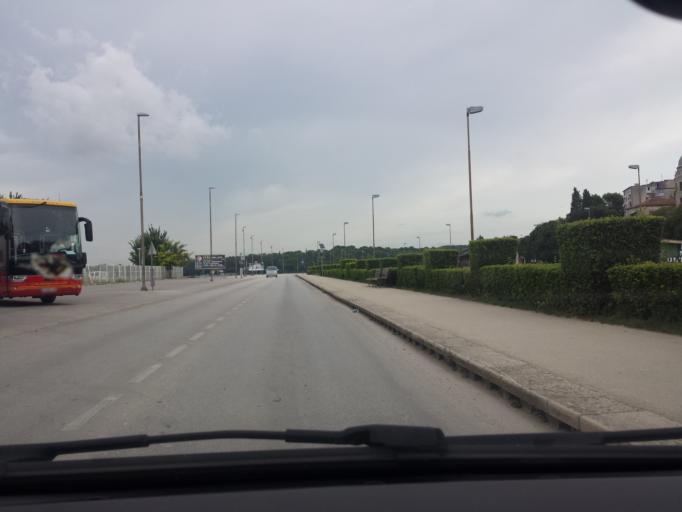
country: HR
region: Istarska
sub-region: Grad Pula
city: Pula
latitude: 44.8766
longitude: 13.8472
